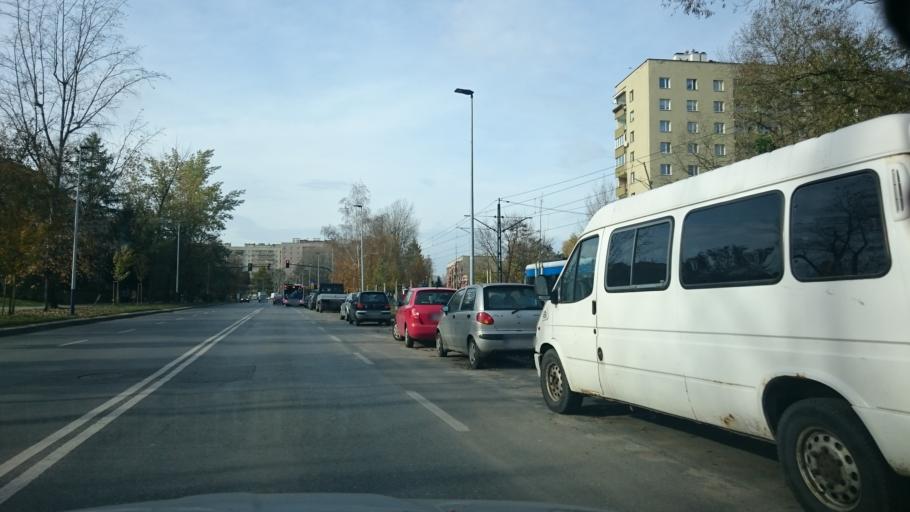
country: PL
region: Lesser Poland Voivodeship
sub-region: Powiat wielicki
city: Czarnochowice
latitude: 50.0162
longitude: 20.0093
